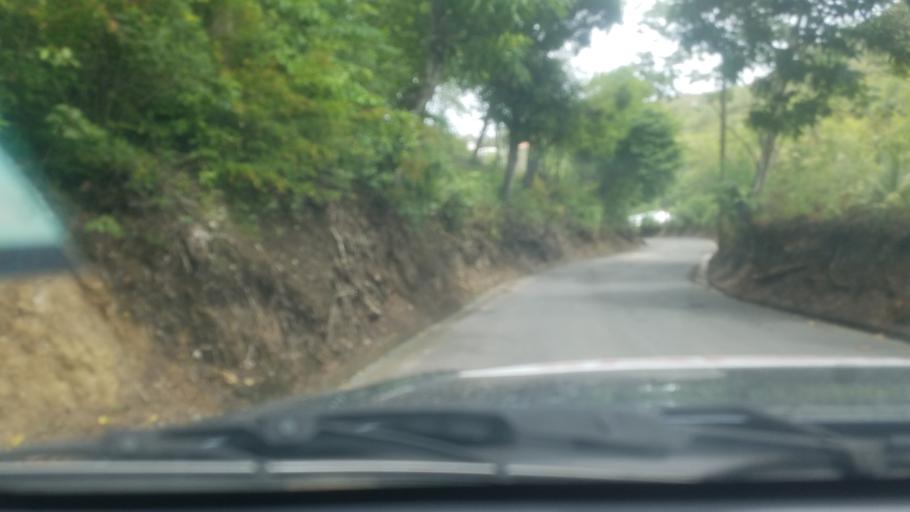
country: LC
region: Laborie Quarter
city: Laborie
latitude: 13.7573
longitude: -60.9886
